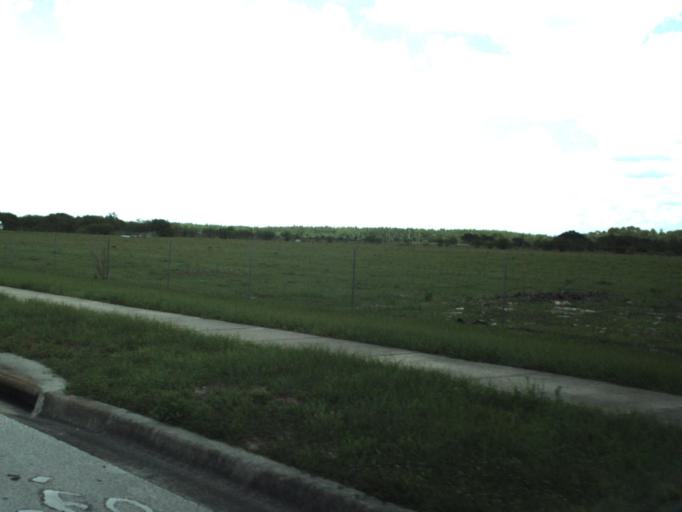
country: US
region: Florida
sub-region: Orange County
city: Conway
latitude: 28.4401
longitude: -81.2587
